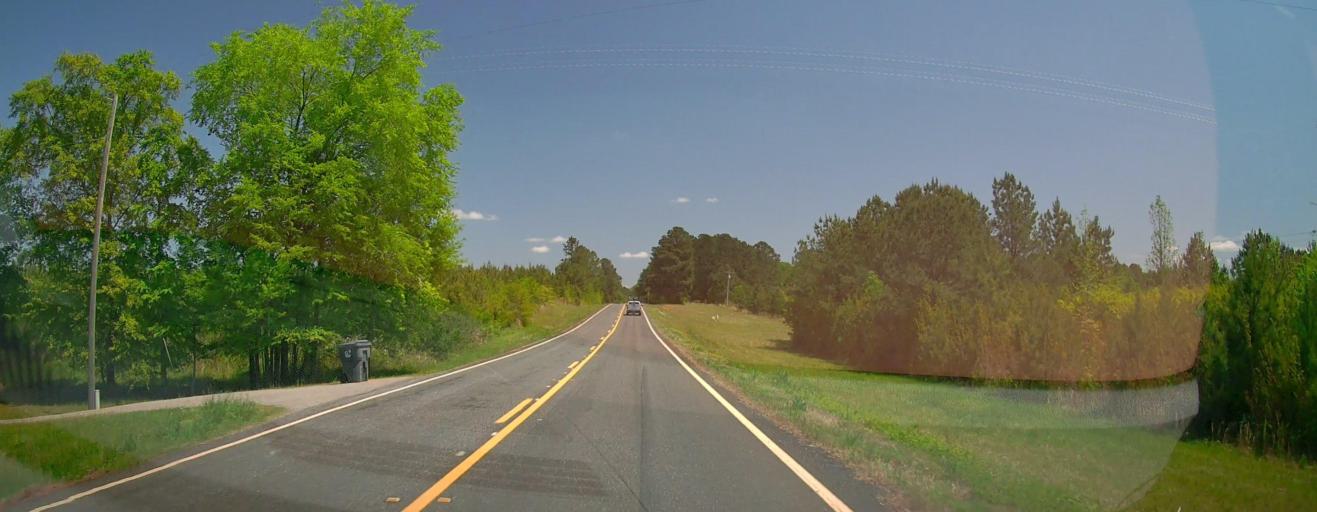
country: US
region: Georgia
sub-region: Jasper County
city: Monticello
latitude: 33.2943
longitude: -83.6557
